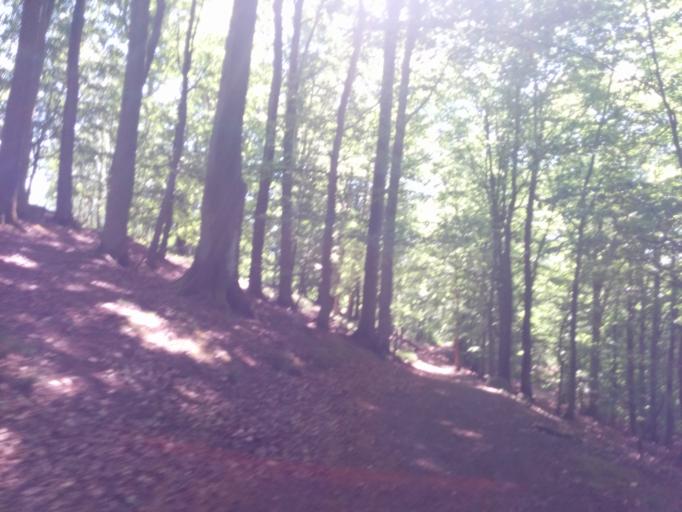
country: SE
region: Skane
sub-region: Lunds Kommun
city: Genarp
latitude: 55.5877
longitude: 13.3871
